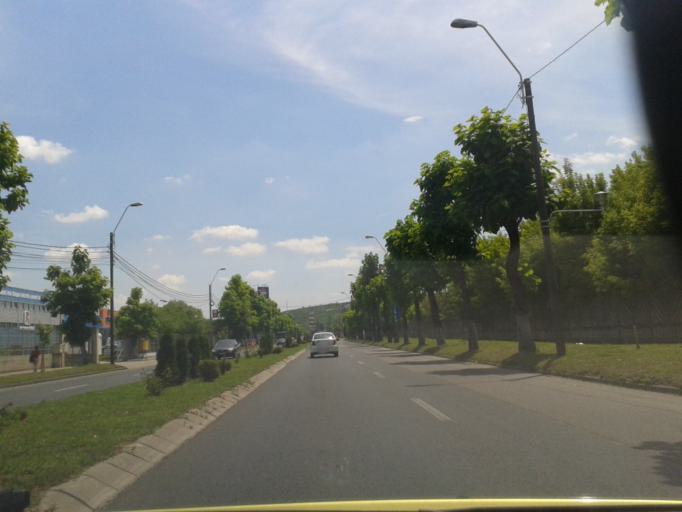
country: RO
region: Hunedoara
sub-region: Municipiul Deva
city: Deva
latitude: 45.8688
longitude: 22.9211
